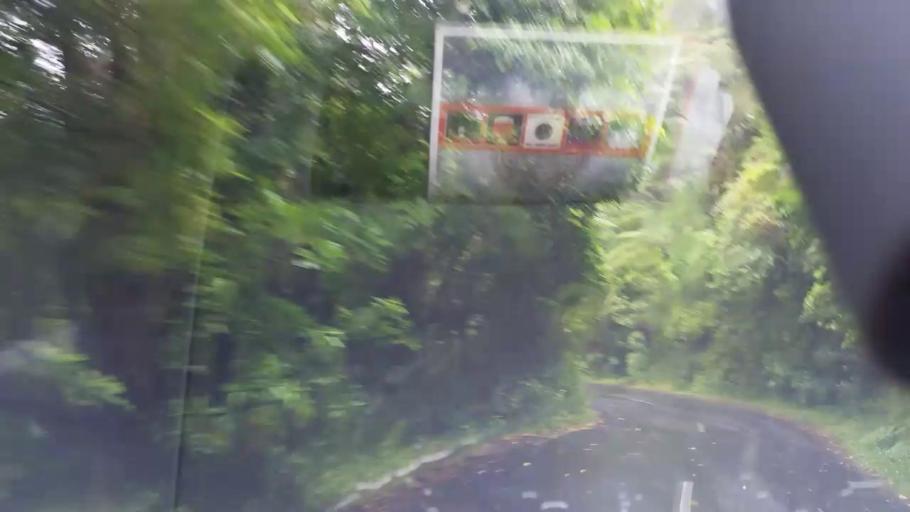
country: NZ
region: Auckland
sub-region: Auckland
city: Waitakere
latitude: -36.9098
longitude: 174.5691
